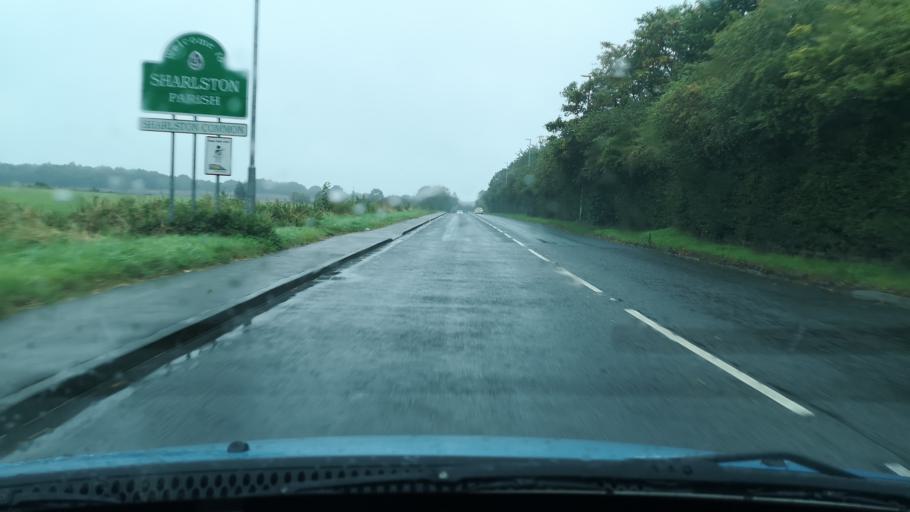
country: GB
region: England
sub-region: City and Borough of Wakefield
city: Sharlston
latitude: 53.6737
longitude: -1.3972
